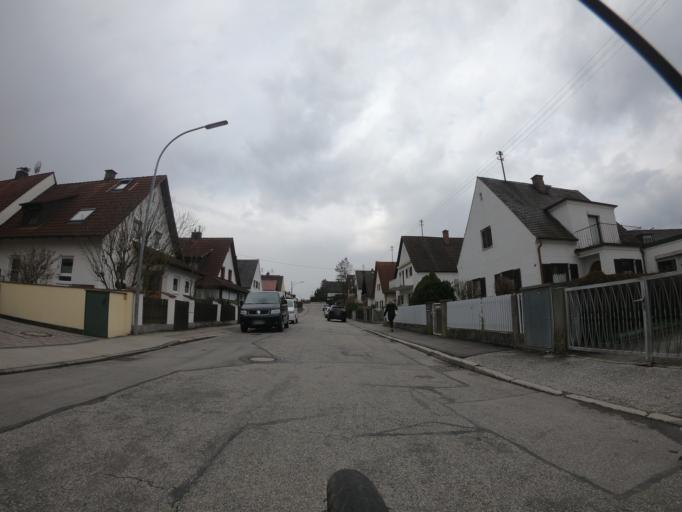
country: DE
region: Bavaria
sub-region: Upper Bavaria
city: Fuerstenfeldbruck
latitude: 48.1775
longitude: 11.2416
